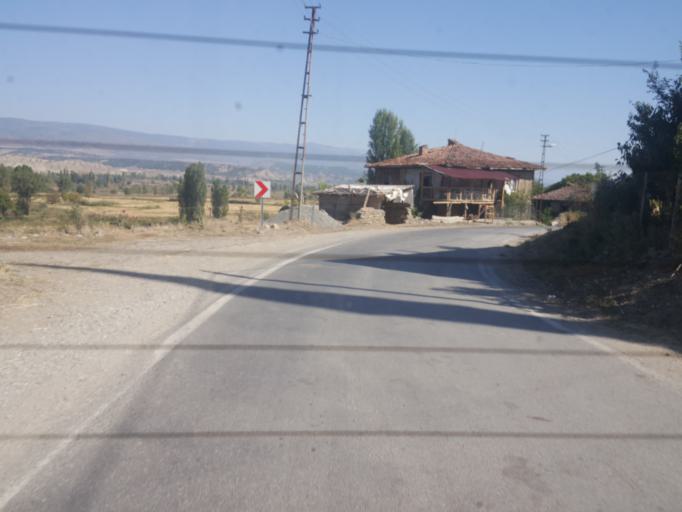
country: TR
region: Kastamonu
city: Tosya
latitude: 40.9866
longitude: 34.1055
